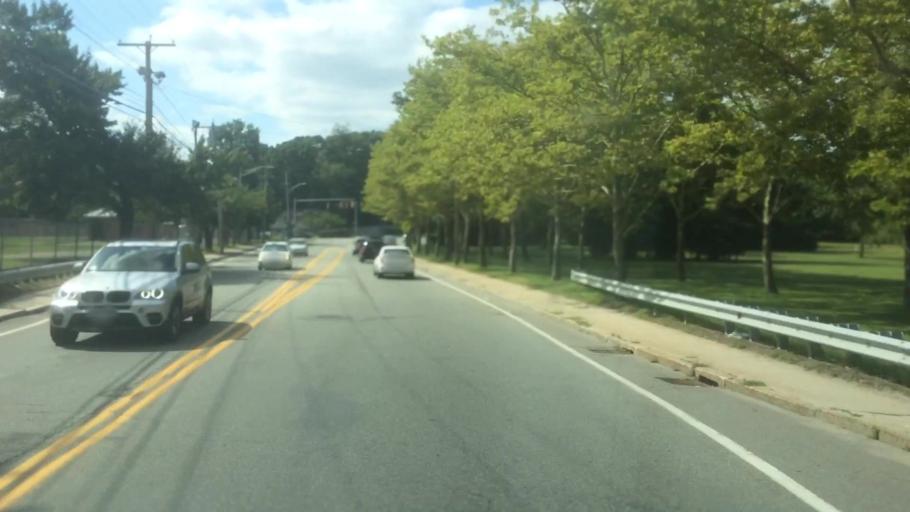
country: US
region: Rhode Island
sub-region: Providence County
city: Cranston
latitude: 41.7727
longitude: -71.4127
